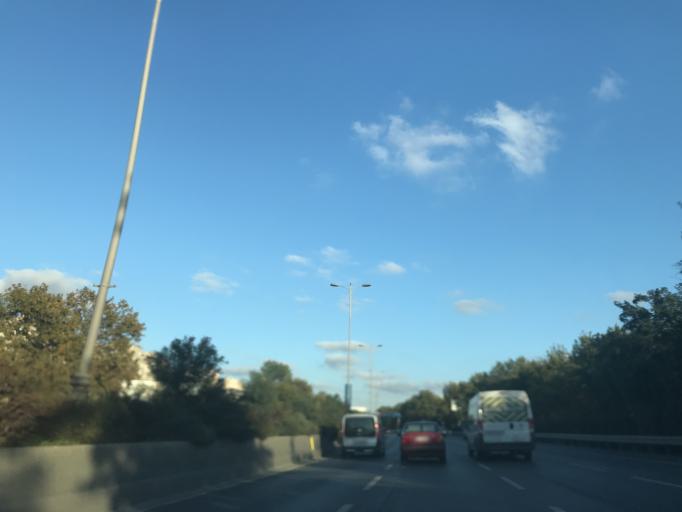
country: TR
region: Istanbul
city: Bagcilar
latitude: 41.0557
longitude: 28.8509
